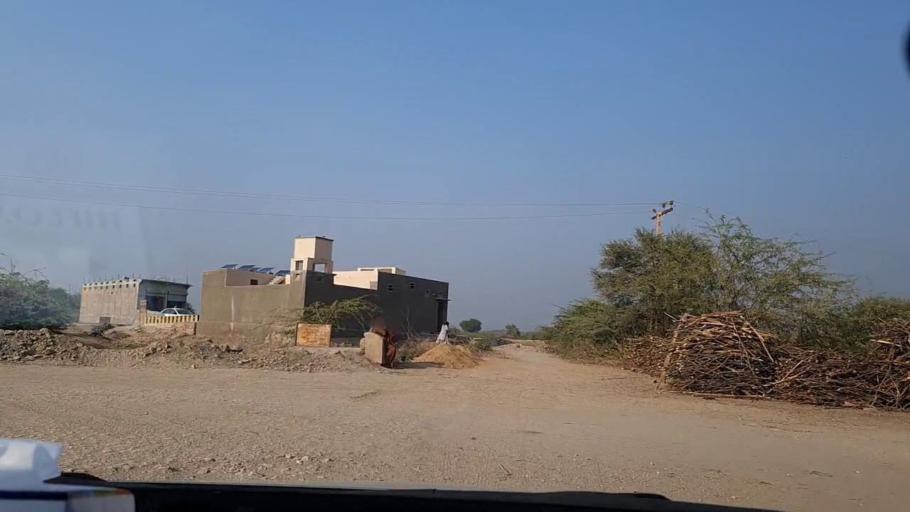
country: PK
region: Sindh
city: Tando Ghulam Ali
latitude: 25.2166
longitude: 68.8759
